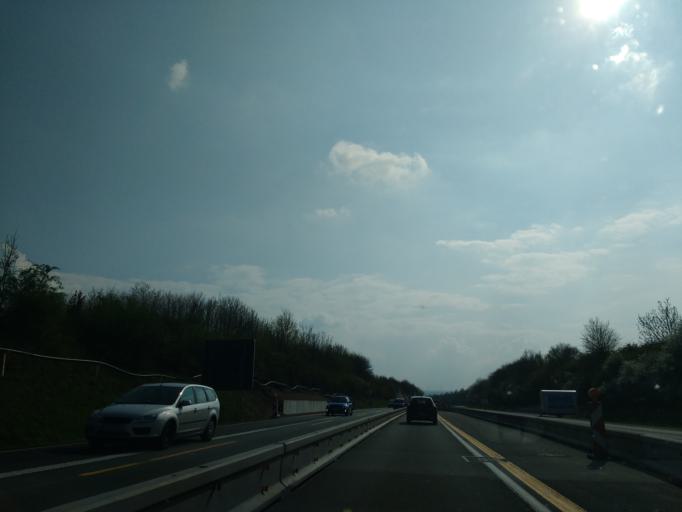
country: DE
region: North Rhine-Westphalia
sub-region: Regierungsbezirk Detmold
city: Paderborn
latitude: 51.6707
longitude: 8.7114
